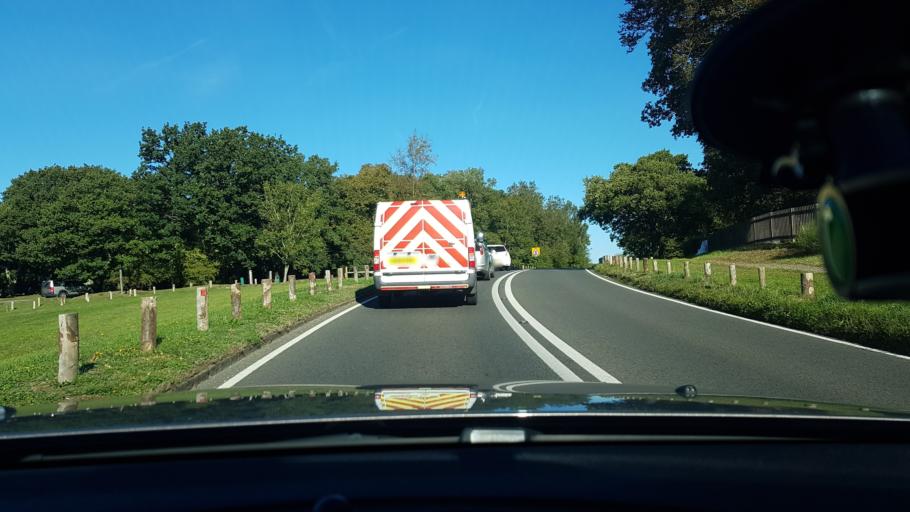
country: GB
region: England
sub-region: Surrey
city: Chilworth
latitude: 51.2324
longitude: -0.5053
